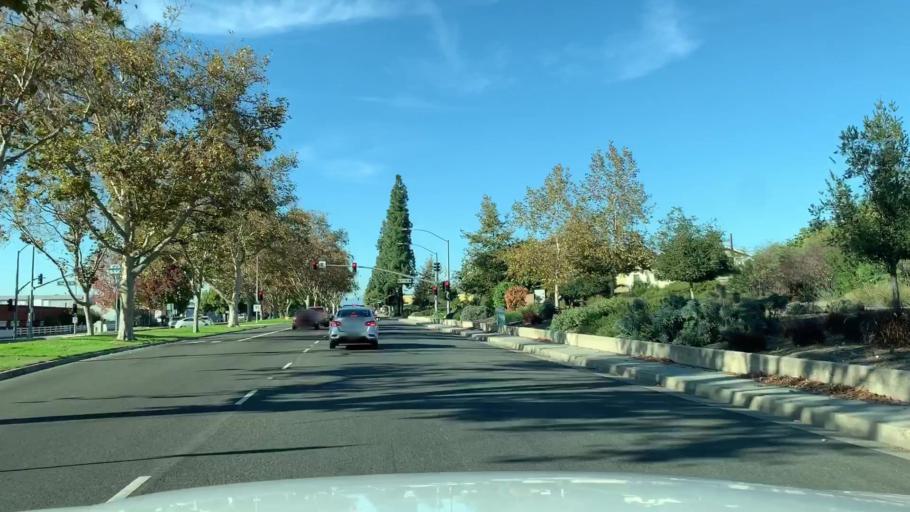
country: US
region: California
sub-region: Los Angeles County
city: South Whittier
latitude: 33.9706
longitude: -118.0435
